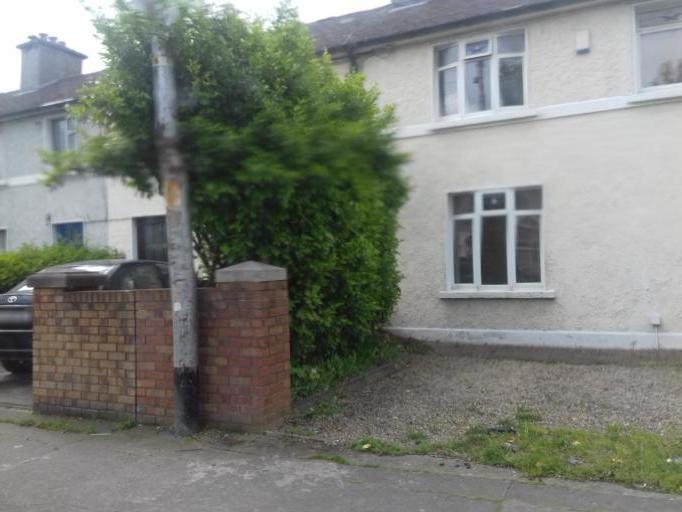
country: IE
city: Greenhills
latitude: 53.3395
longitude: -6.3108
